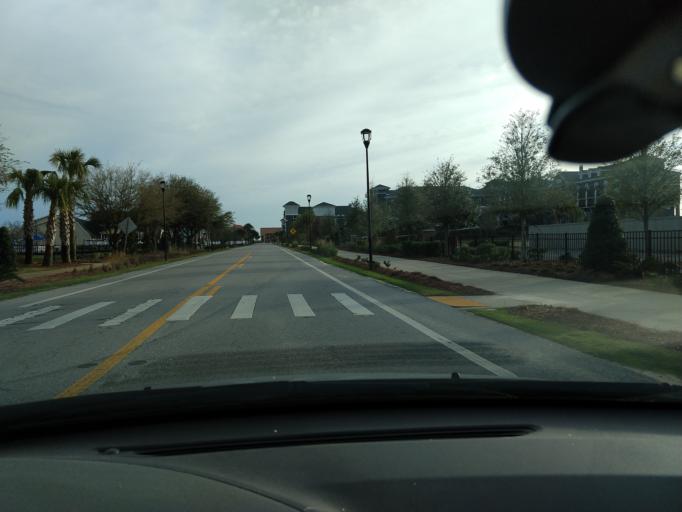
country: US
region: Florida
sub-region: Okaloosa County
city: Destin
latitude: 30.3864
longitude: -86.4304
